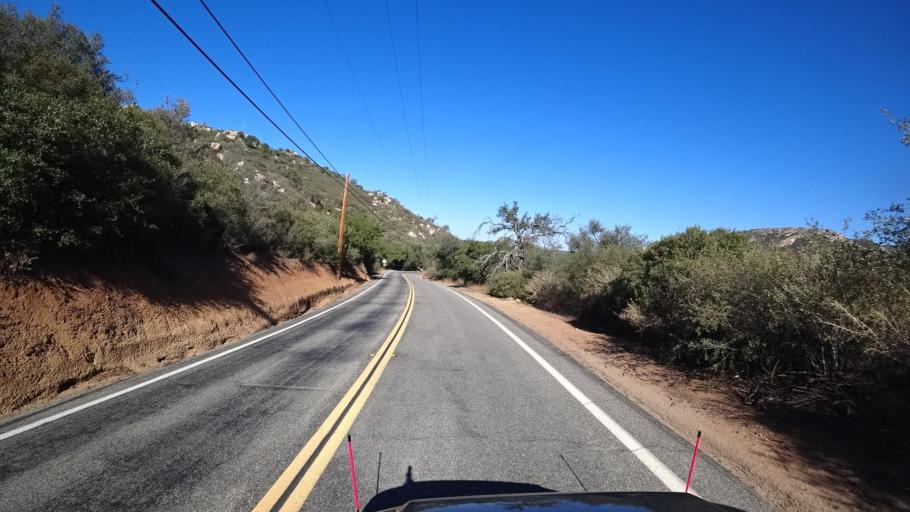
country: US
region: California
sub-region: San Diego County
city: Jamul
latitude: 32.7036
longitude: -116.7460
